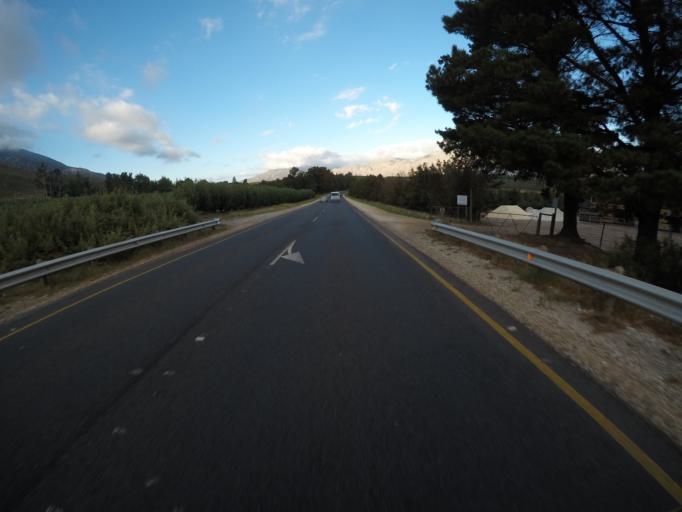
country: ZA
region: Western Cape
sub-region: Overberg District Municipality
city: Grabouw
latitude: -34.0164
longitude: 19.2450
